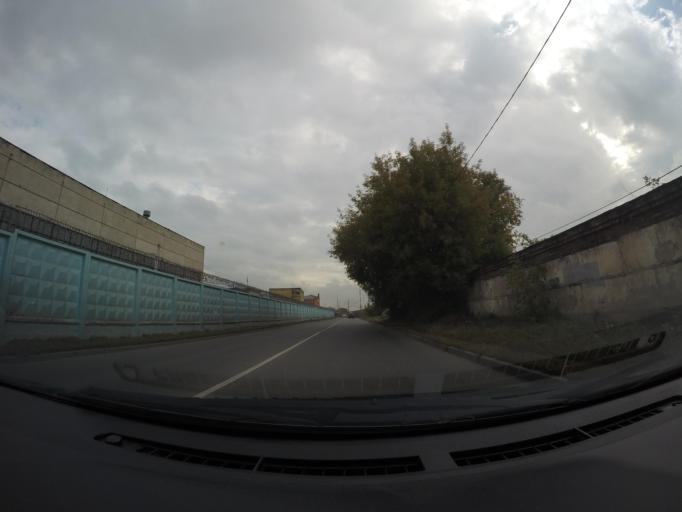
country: RU
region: Moscow
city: Lefortovo
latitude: 55.7680
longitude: 37.7212
